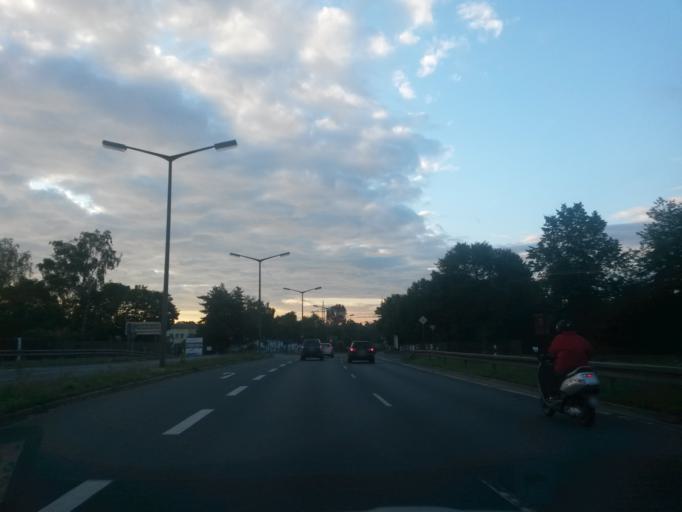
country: DE
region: Bavaria
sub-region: Regierungsbezirk Mittelfranken
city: Oberasbach
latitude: 49.4369
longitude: 10.9841
